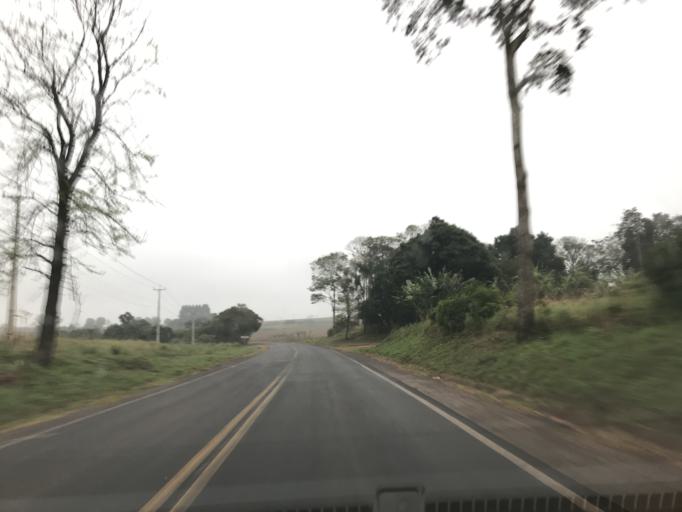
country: PY
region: Canindeyu
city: Salto del Guaira
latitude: -24.1296
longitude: -54.1135
